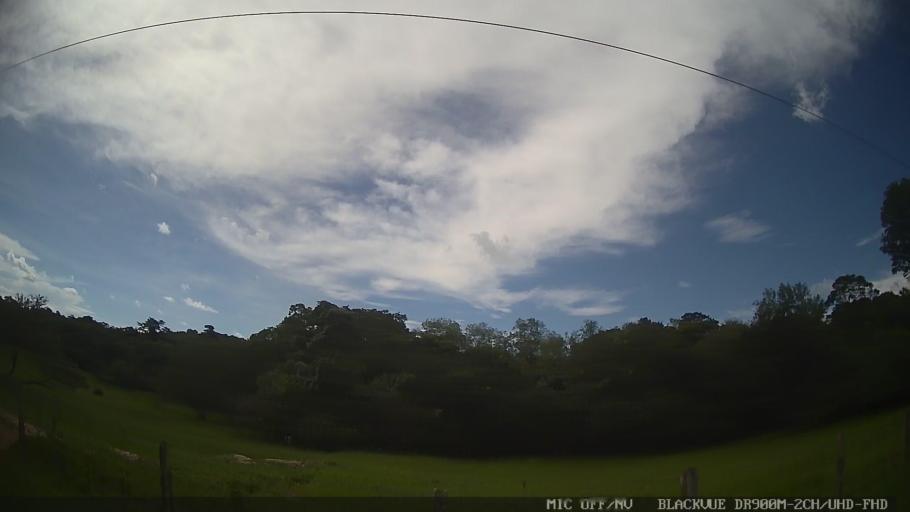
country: BR
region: Sao Paulo
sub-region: Conchas
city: Conchas
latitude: -22.9892
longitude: -47.9951
